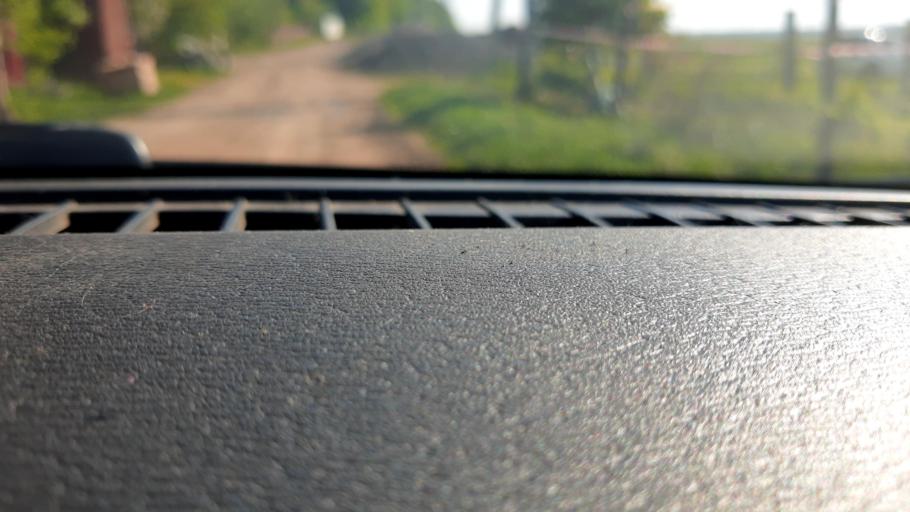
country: RU
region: Bashkortostan
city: Iglino
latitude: 54.7613
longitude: 56.4211
